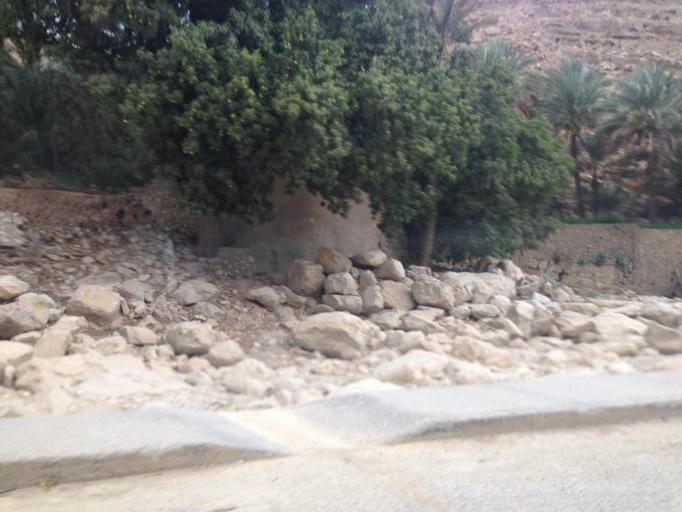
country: OM
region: Ash Sharqiyah
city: Badiyah
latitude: 22.6147
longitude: 59.0940
